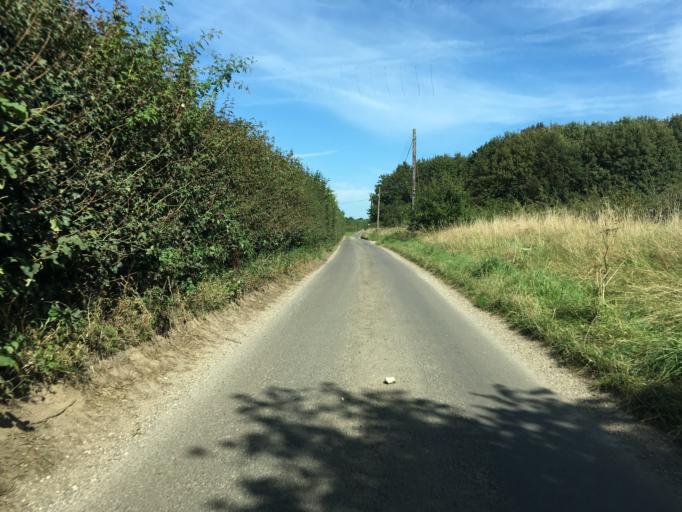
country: GB
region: England
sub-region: Hampshire
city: Highclere
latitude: 51.3051
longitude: -1.3841
